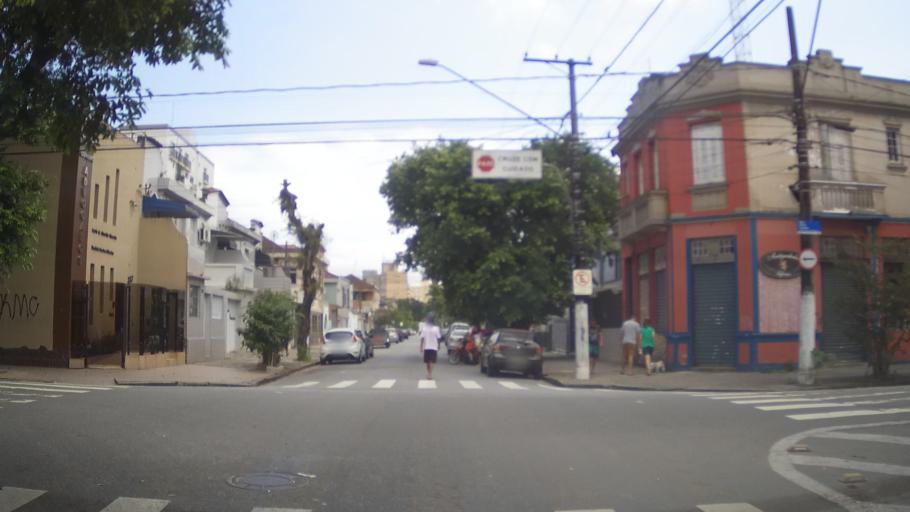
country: BR
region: Sao Paulo
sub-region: Santos
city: Santos
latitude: -23.9535
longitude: -46.3196
